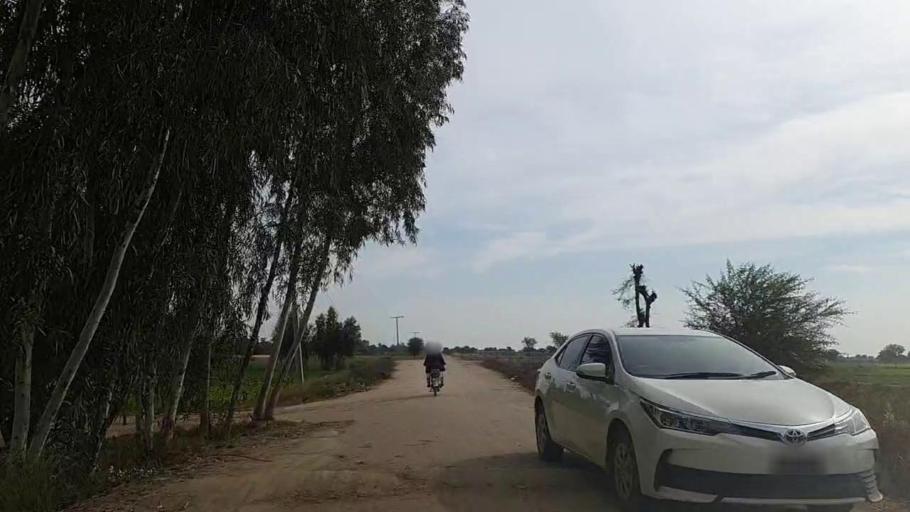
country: PK
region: Sindh
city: Daur
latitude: 26.4230
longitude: 68.4848
